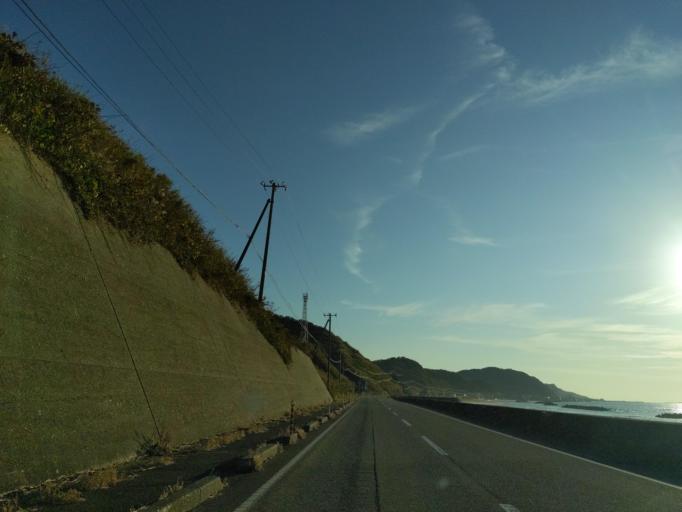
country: JP
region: Niigata
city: Nagaoka
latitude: 37.5620
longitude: 138.7164
